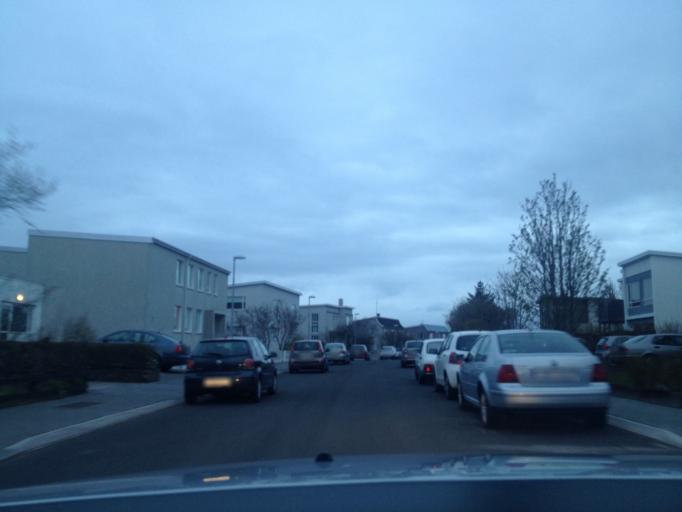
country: IS
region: Capital Region
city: Seltjarnarnes
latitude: 64.1524
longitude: -21.9992
